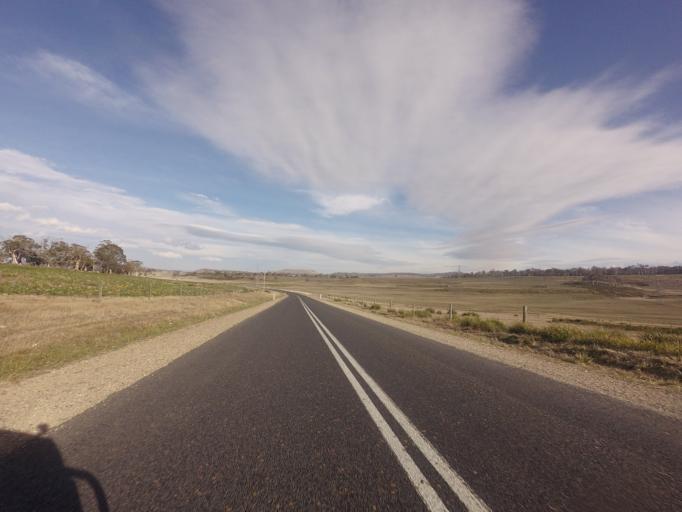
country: AU
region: Tasmania
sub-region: Derwent Valley
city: New Norfolk
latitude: -42.2464
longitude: 146.9257
